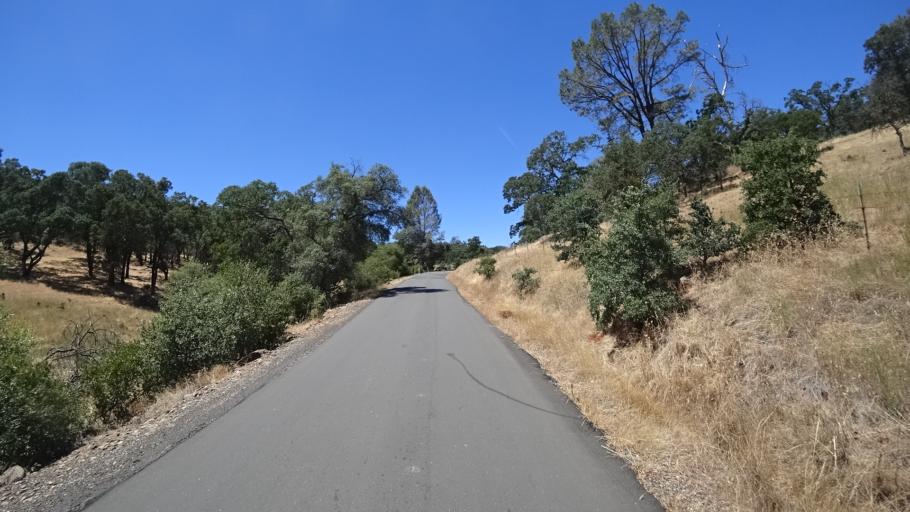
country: US
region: California
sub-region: Calaveras County
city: Rancho Calaveras
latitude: 38.0498
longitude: -120.7835
